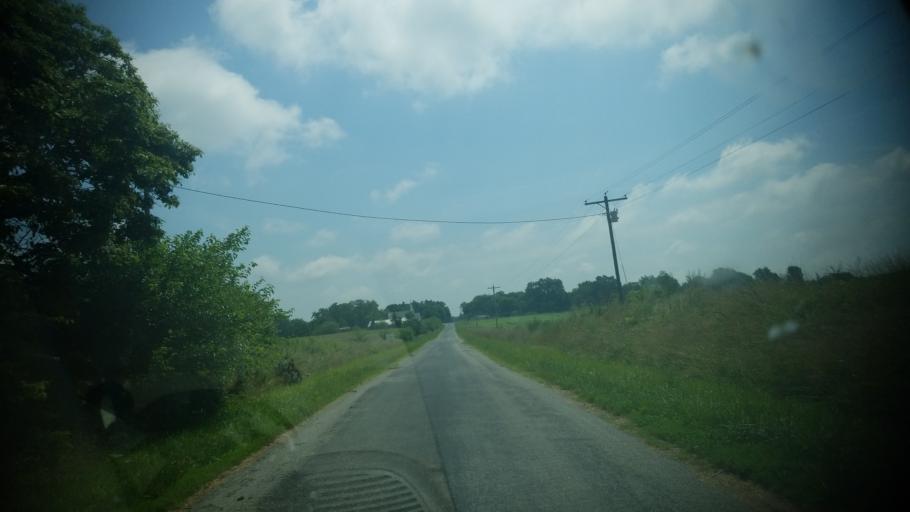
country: US
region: Illinois
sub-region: Wayne County
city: Fairfield
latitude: 38.5223
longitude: -88.3630
